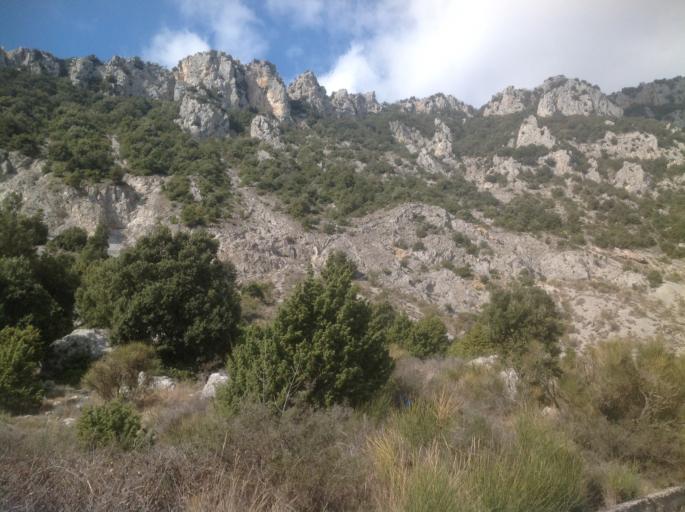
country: IT
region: Calabria
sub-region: Provincia di Cosenza
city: Civita
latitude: 39.8326
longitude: 16.3021
